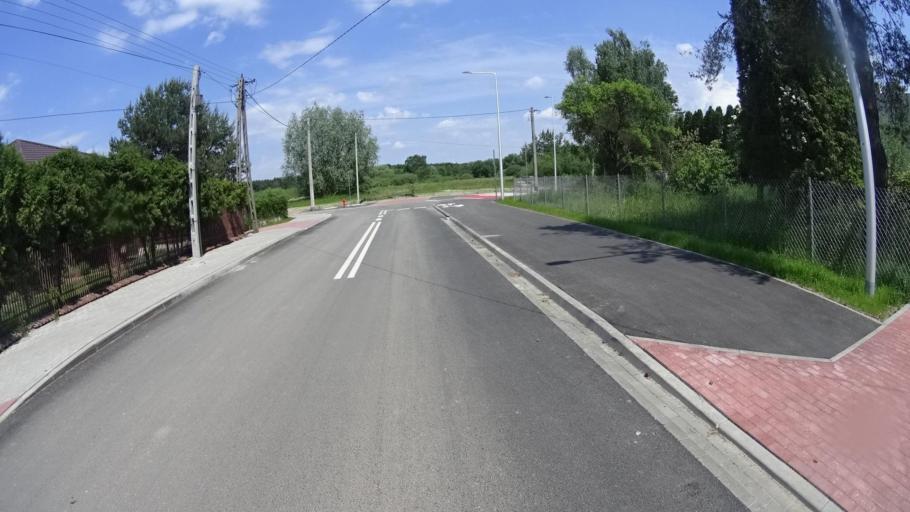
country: PL
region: Masovian Voivodeship
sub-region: Powiat warszawski zachodni
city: Stare Babice
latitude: 52.2668
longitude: 20.8451
